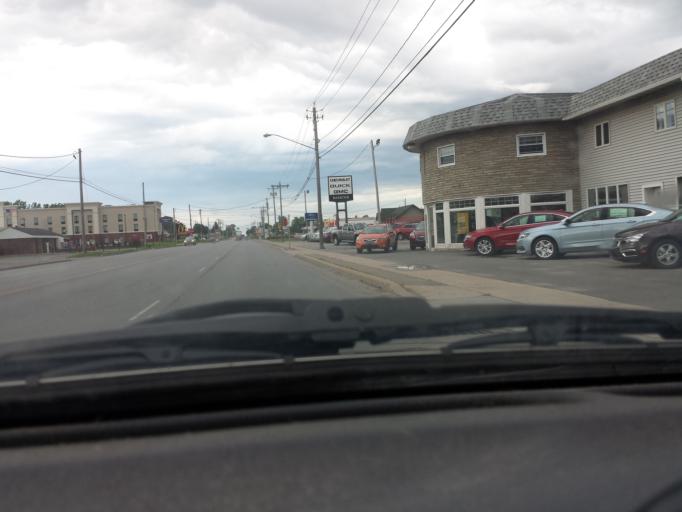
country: US
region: New York
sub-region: St. Lawrence County
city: Potsdam
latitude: 44.6808
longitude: -74.9869
